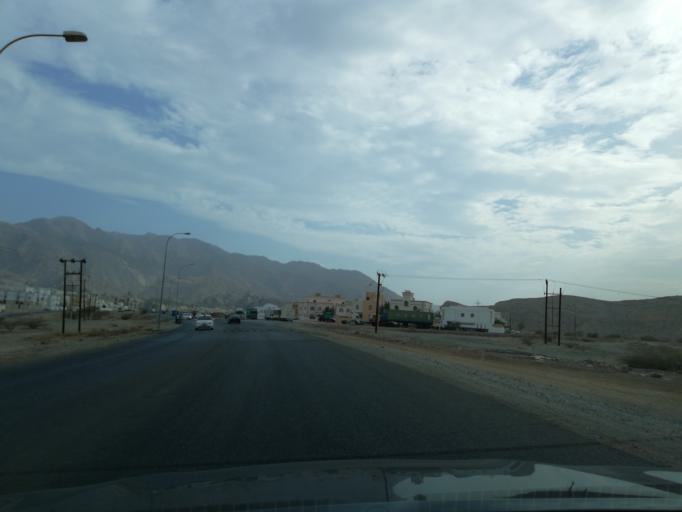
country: OM
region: Muhafazat Masqat
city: Bawshar
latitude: 23.4879
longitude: 58.3142
